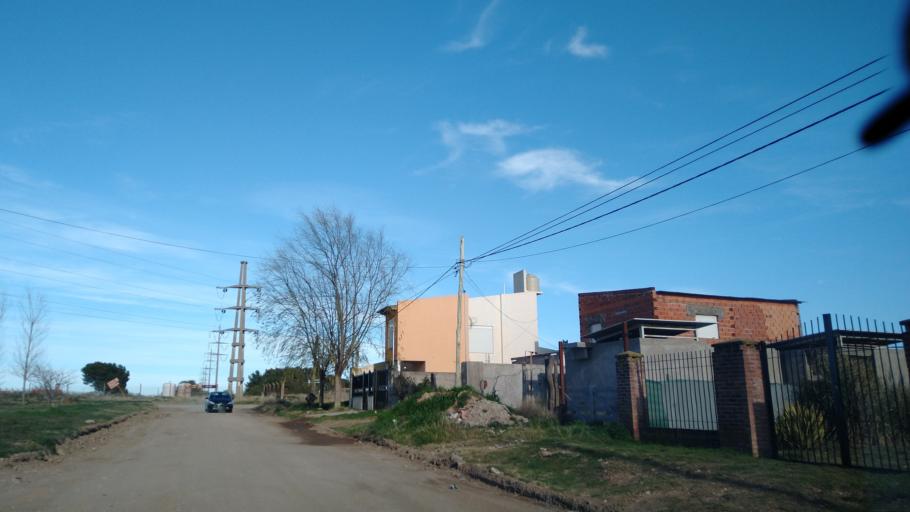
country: AR
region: Buenos Aires
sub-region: Partido de Bahia Blanca
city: Bahia Blanca
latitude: -38.7044
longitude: -62.2074
